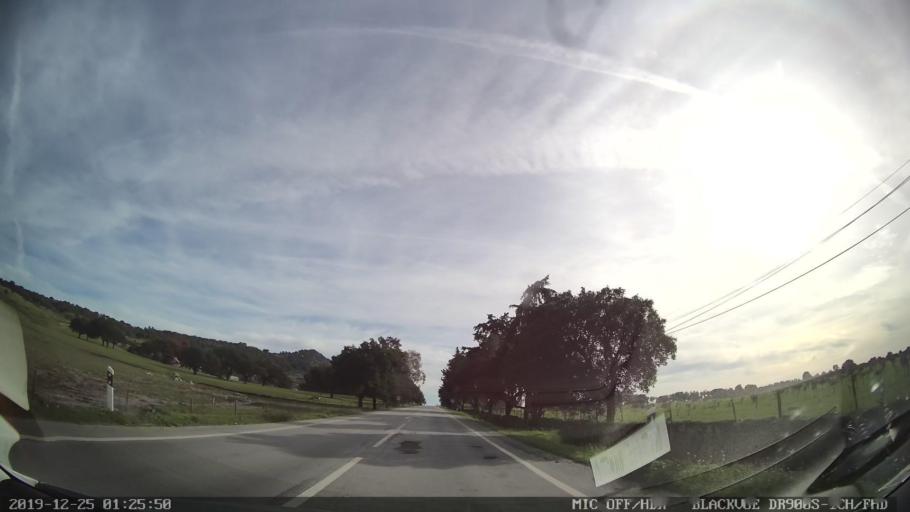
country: PT
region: Portalegre
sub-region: Portalegre
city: Fortios
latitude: 39.3081
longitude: -7.4672
